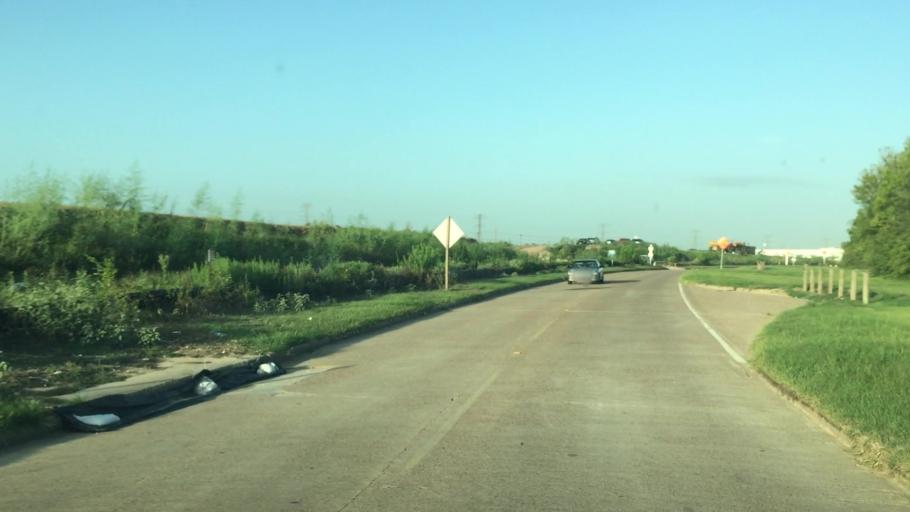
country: US
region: Texas
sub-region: Harris County
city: Hudson
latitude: 29.9437
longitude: -95.4756
